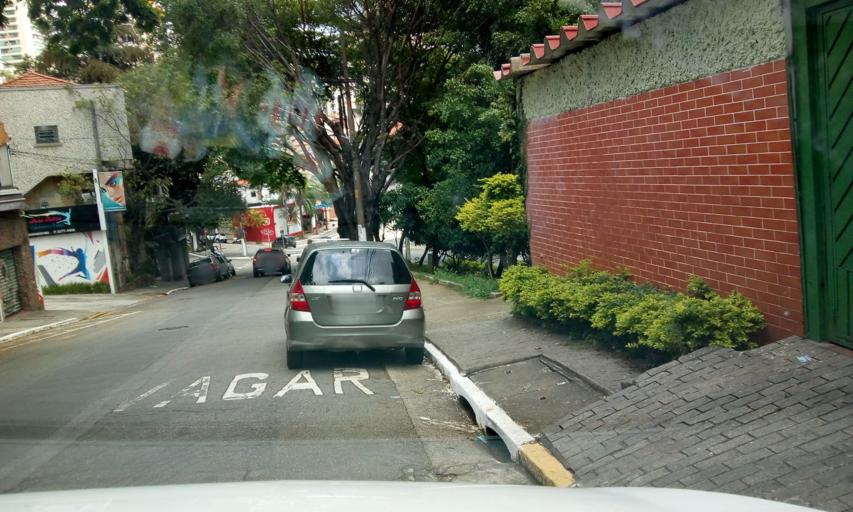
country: BR
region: Sao Paulo
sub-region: Sao Paulo
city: Sao Paulo
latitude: -23.5751
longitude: -46.6344
